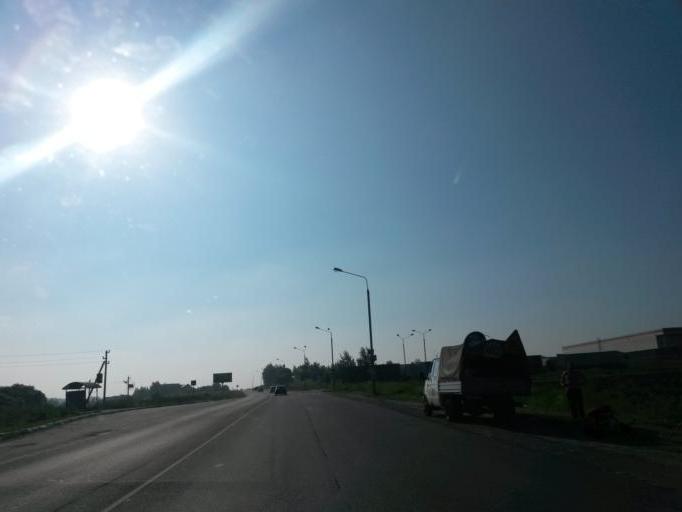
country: RU
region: Moskovskaya
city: Yam
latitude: 55.4841
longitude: 37.7616
